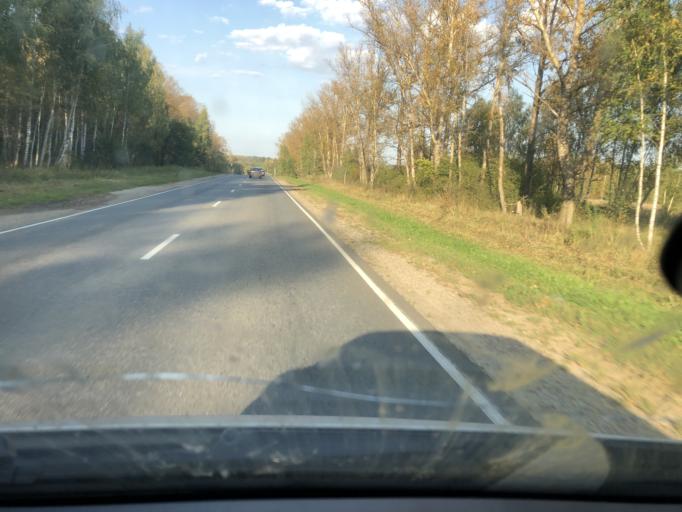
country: RU
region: Kaluga
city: Peremyshl'
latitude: 54.2233
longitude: 36.0349
